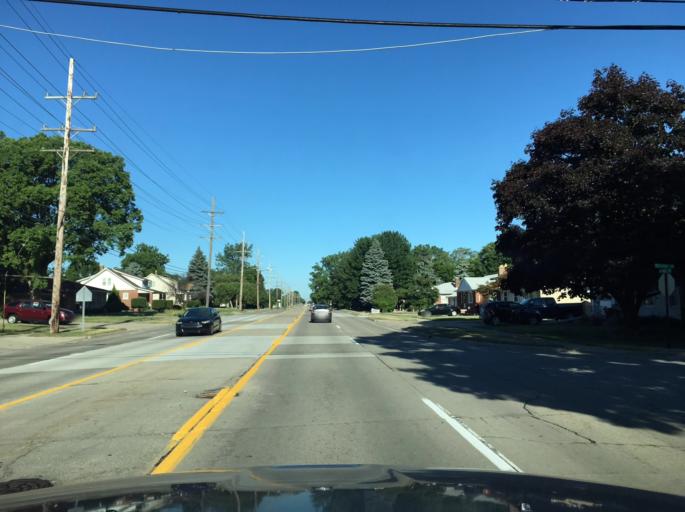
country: US
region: Michigan
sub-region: Macomb County
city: Fraser
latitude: 42.5388
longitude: -82.9567
